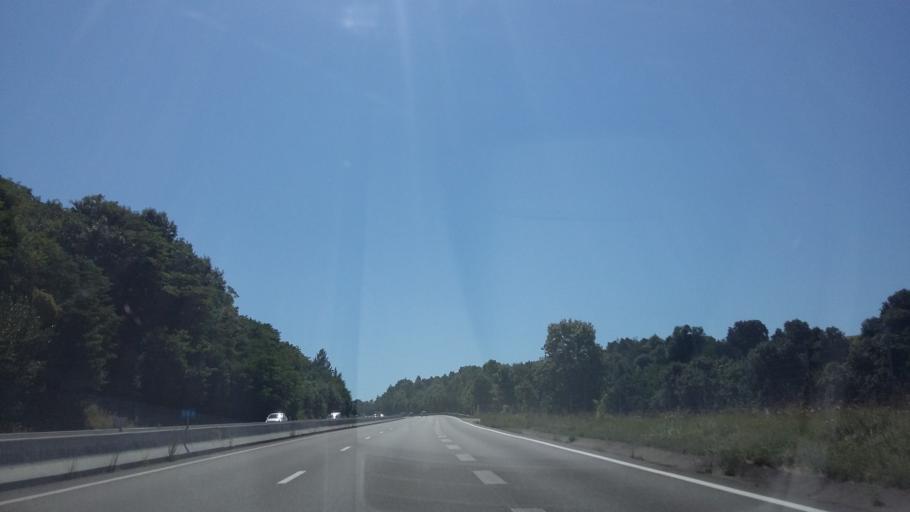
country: FR
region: Rhone-Alpes
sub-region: Departement de l'Isere
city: Chabons
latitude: 45.4674
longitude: 5.4013
